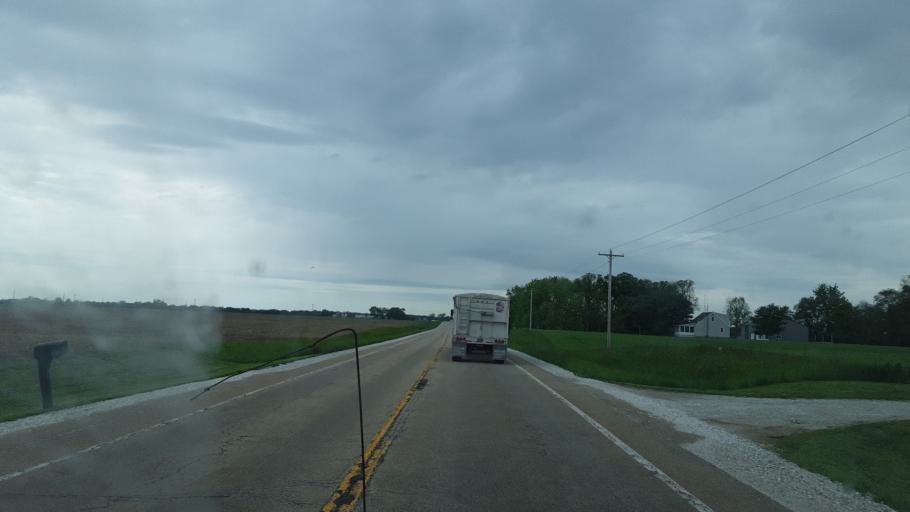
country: US
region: Illinois
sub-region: Fulton County
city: Lewistown
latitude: 40.3311
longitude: -90.1904
